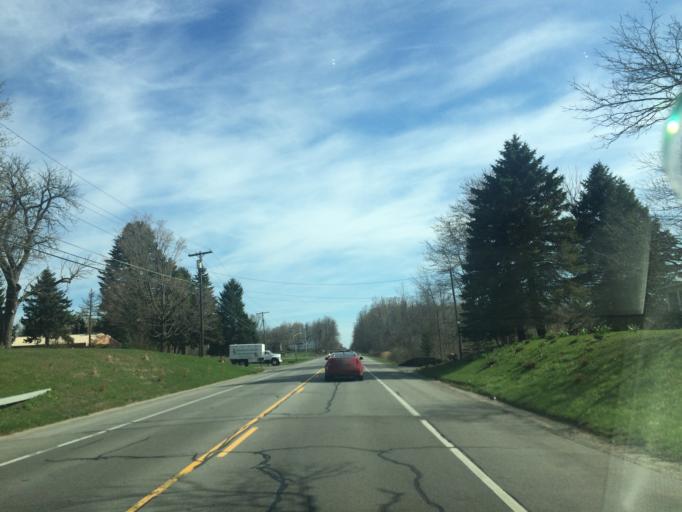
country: US
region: New York
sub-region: Monroe County
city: Webster
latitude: 43.1799
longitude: -77.4308
